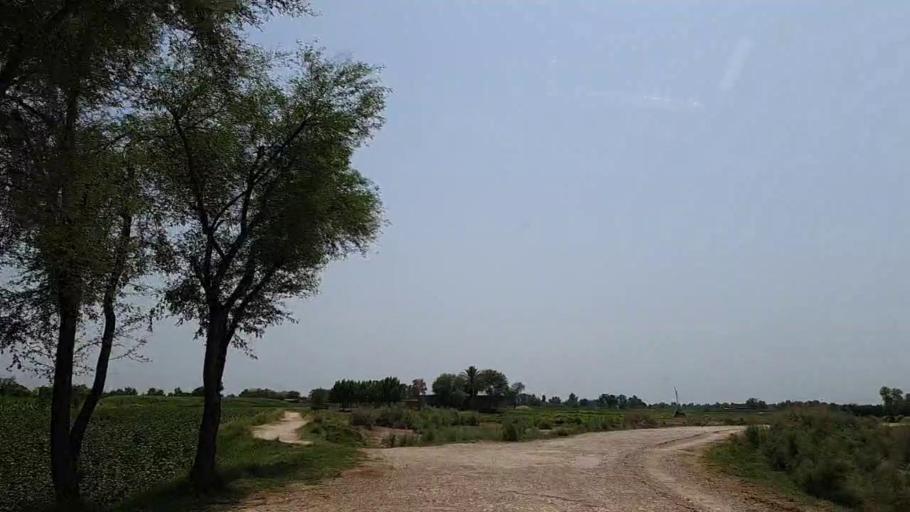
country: PK
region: Sindh
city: Adilpur
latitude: 27.9718
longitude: 69.3975
